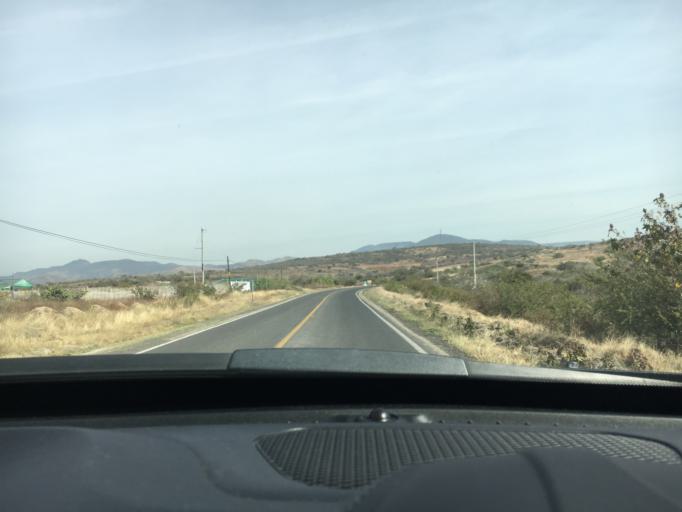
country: MX
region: Guanajuato
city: Duarte
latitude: 21.0537
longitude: -101.5119
